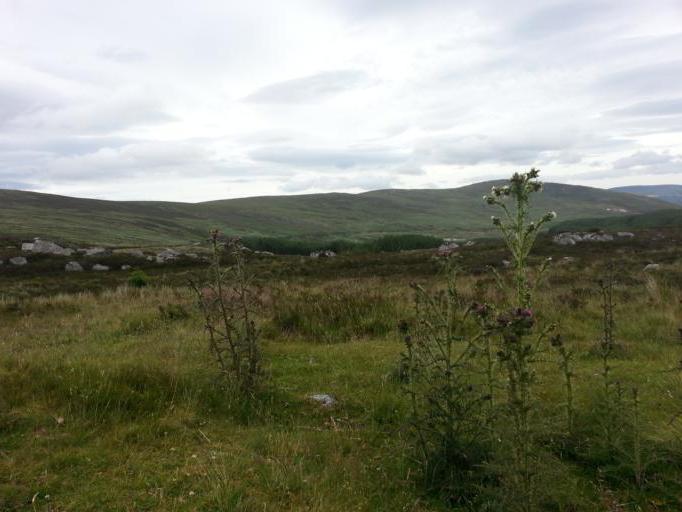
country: IE
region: Leinster
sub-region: Wicklow
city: Valleymount
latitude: 53.0408
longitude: -6.3977
